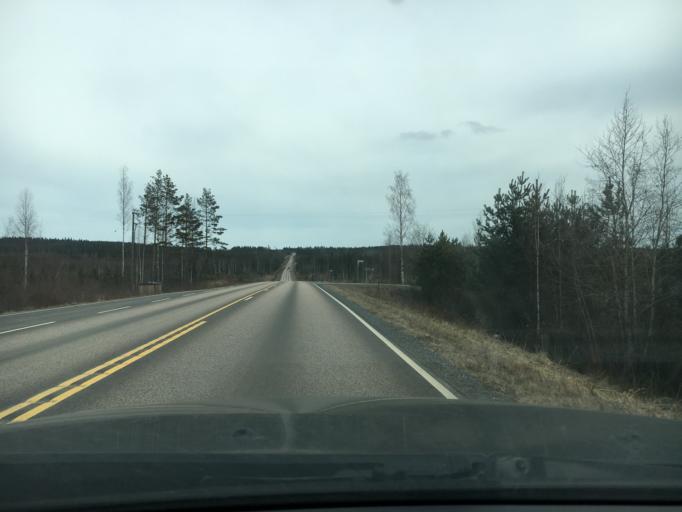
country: FI
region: Central Finland
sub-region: AEaenekoski
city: Konnevesi
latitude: 62.6886
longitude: 26.4020
